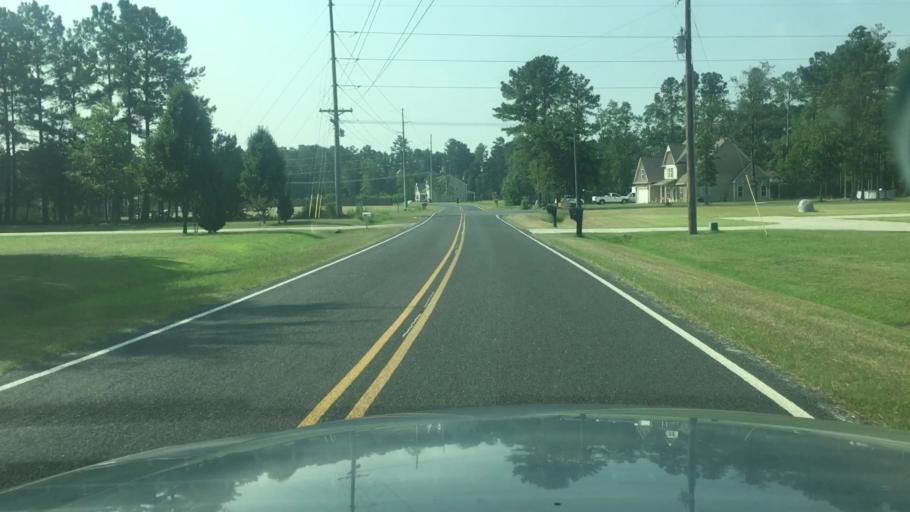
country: US
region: North Carolina
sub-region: Cumberland County
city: Hope Mills
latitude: 34.9041
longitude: -78.8720
